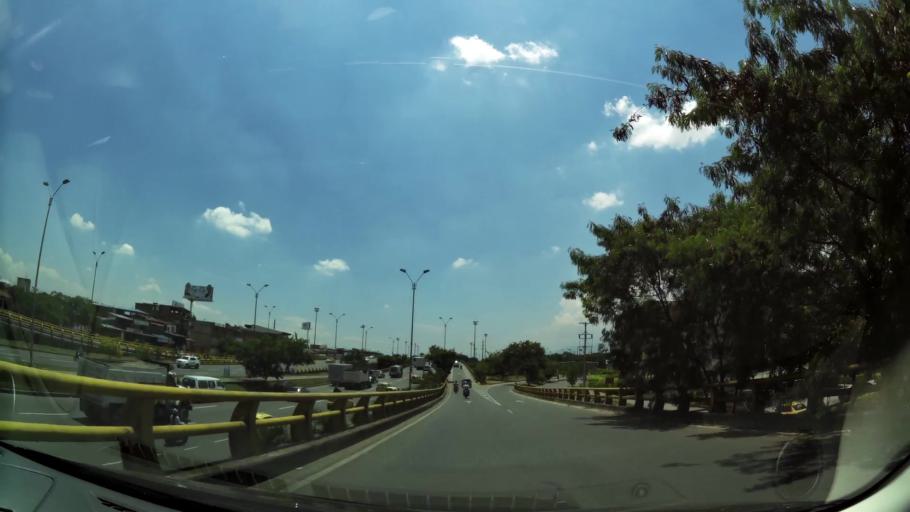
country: CO
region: Valle del Cauca
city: Cali
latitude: 3.4544
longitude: -76.4857
